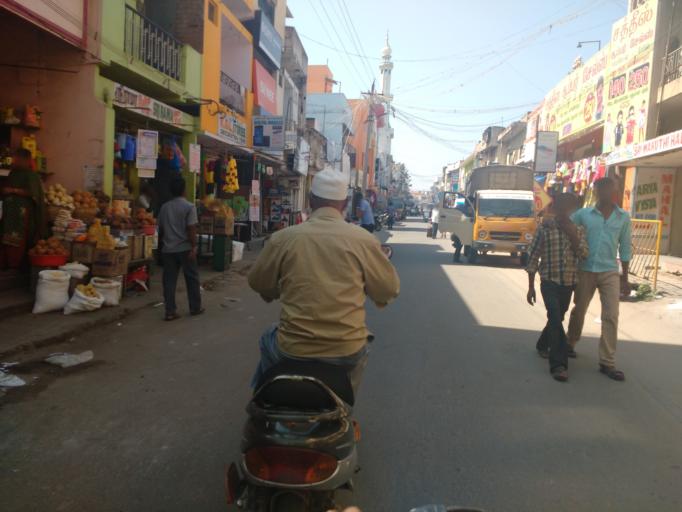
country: IN
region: Tamil Nadu
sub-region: Krishnagiri
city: Hosur
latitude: 12.7327
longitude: 77.8284
